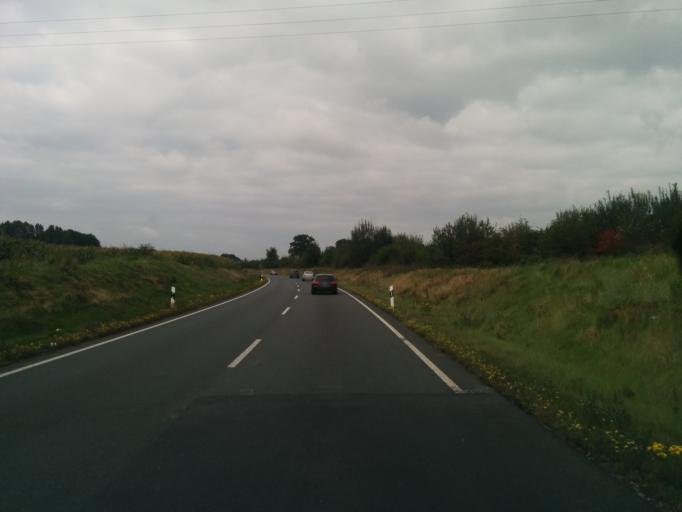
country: DE
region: North Rhine-Westphalia
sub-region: Regierungsbezirk Munster
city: Coesfeld
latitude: 51.9054
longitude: 7.1945
